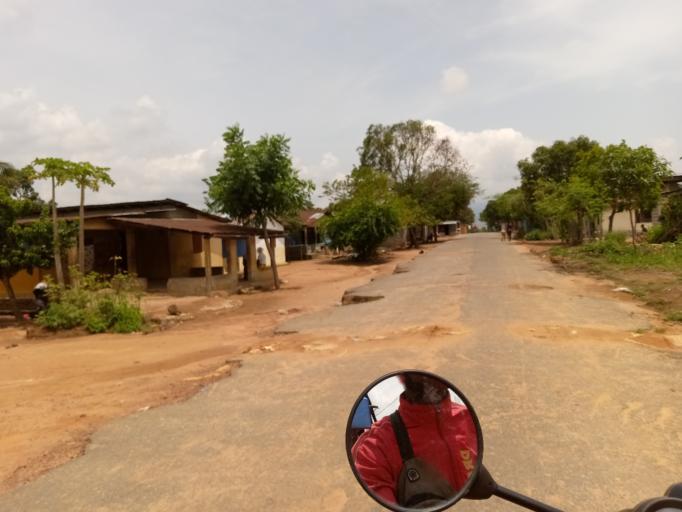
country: SL
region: Western Area
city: Waterloo
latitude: 8.3344
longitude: -13.0217
